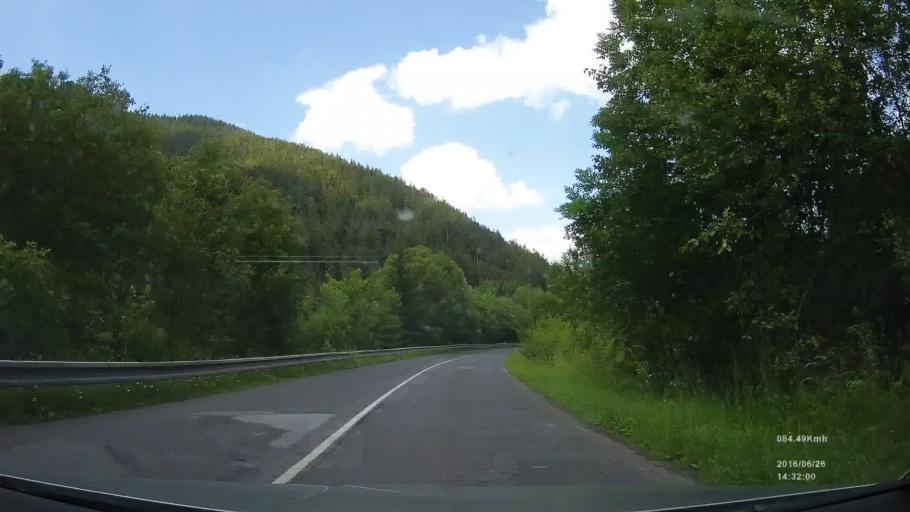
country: SK
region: Zilinsky
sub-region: Okres Zilina
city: Liptovsky Hradok
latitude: 49.0077
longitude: 19.7669
